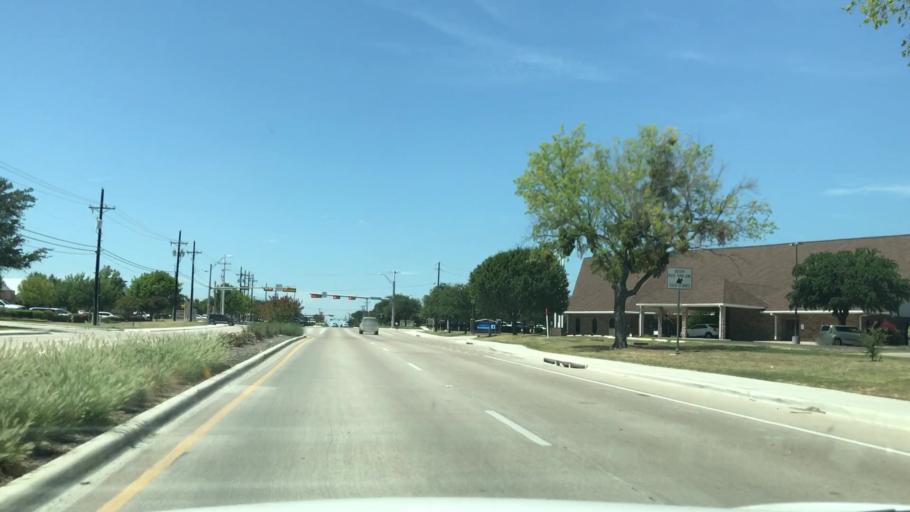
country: US
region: Texas
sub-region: Rockwall County
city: Rockwall
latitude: 32.8883
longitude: -96.4673
